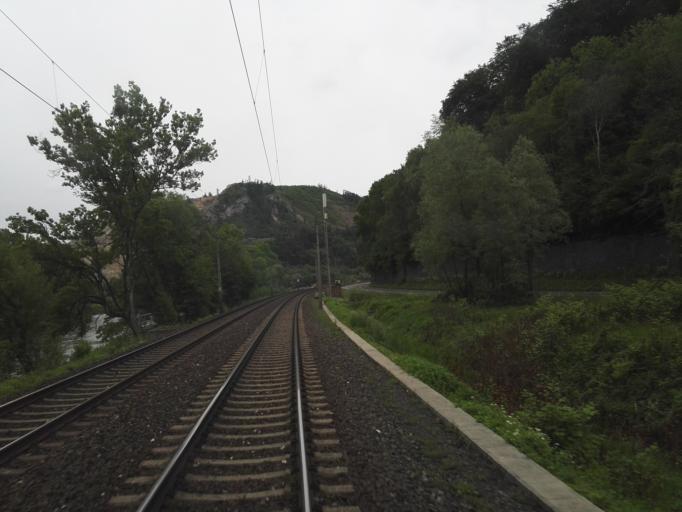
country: AT
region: Styria
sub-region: Politischer Bezirk Graz-Umgebung
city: Gratkorn
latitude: 47.1184
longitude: 15.3641
